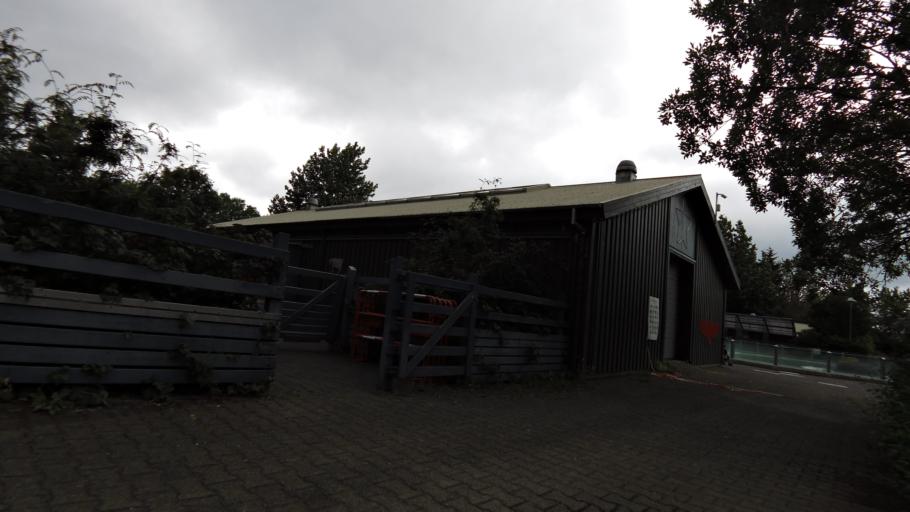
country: IS
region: Capital Region
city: Reykjavik
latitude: 64.1390
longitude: -21.8711
